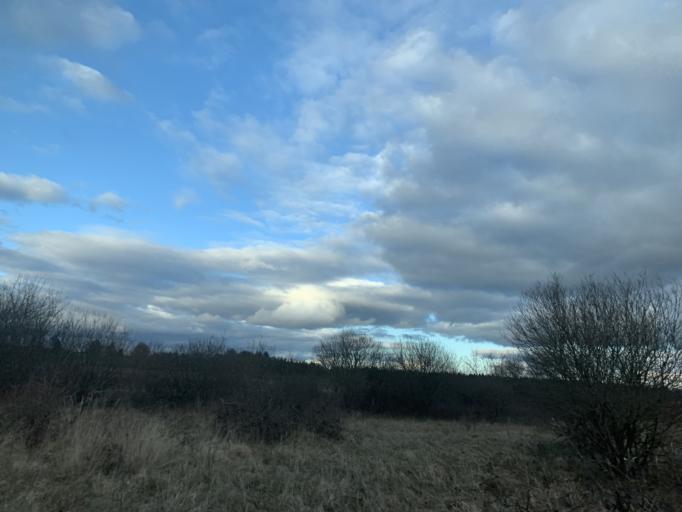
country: IE
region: Connaught
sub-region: Maigh Eo
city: Ballyhaunis
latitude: 53.8481
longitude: -8.7319
